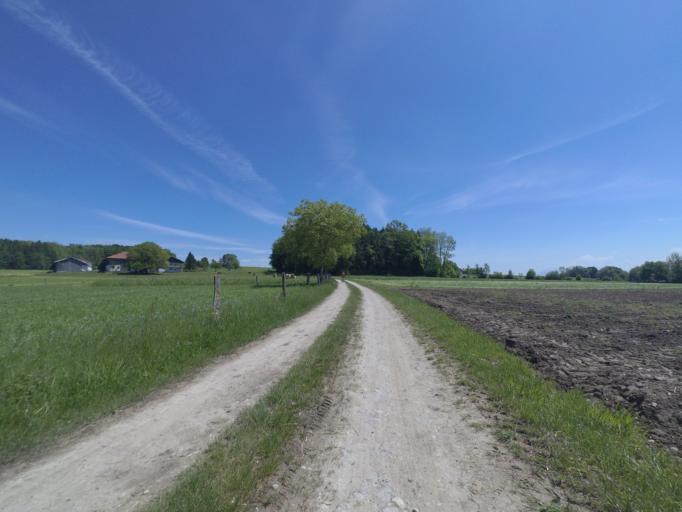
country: DE
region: Bavaria
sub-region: Upper Bavaria
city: Petting
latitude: 47.9487
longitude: 12.7859
